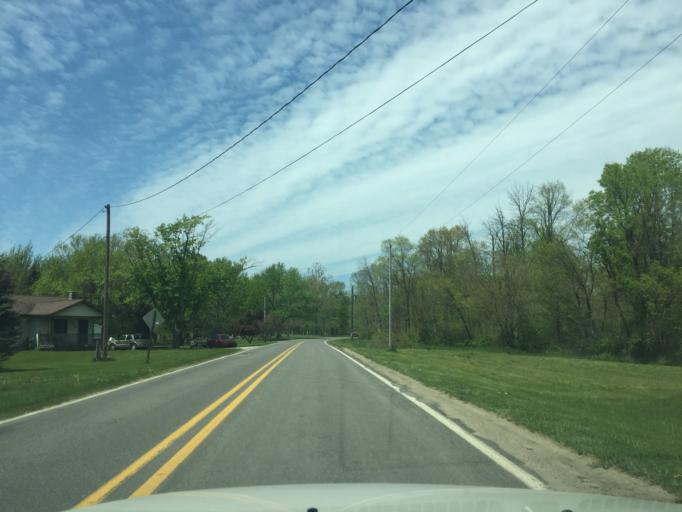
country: US
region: Michigan
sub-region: Berrien County
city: Stevensville
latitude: 41.9640
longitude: -86.4885
